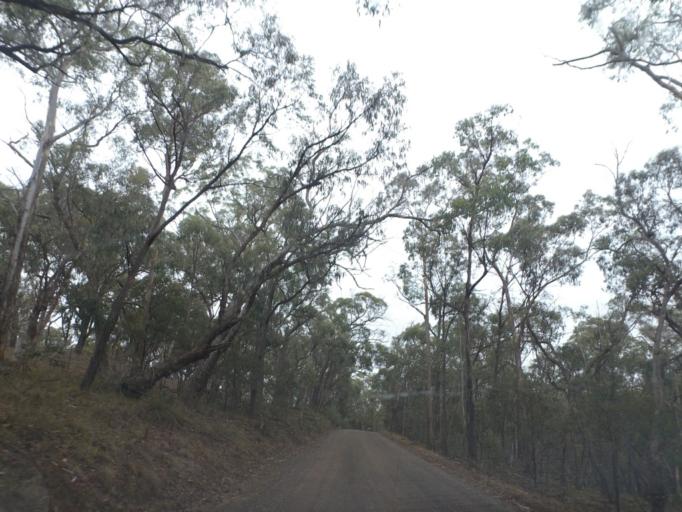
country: AU
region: Victoria
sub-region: Nillumbik
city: Saint Andrews
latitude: -37.6134
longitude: 145.2897
